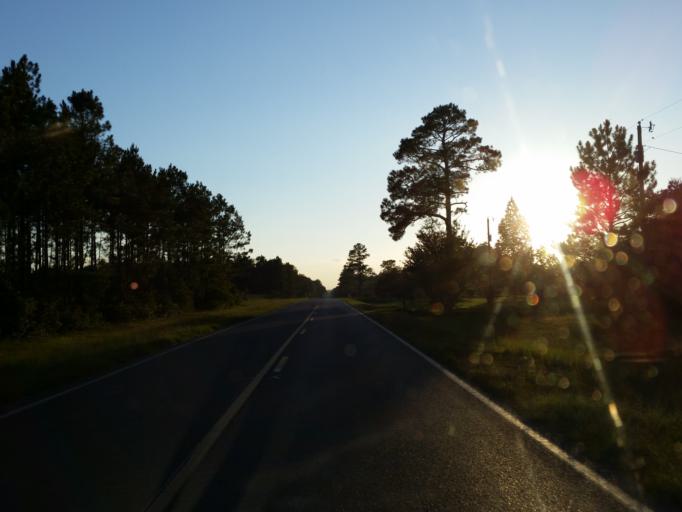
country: US
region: Georgia
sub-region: Berrien County
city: Nashville
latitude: 31.1860
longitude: -83.1519
